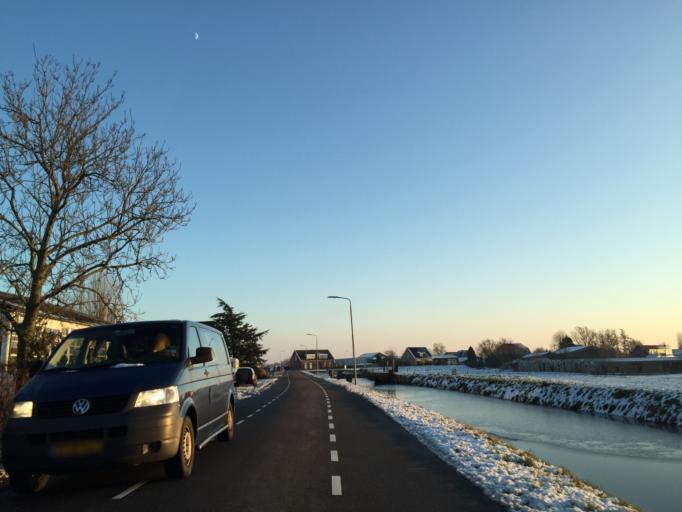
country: NL
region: South Holland
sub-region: Gemeente Pijnacker-Nootdorp
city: Pijnacker
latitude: 51.9981
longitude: 4.4399
